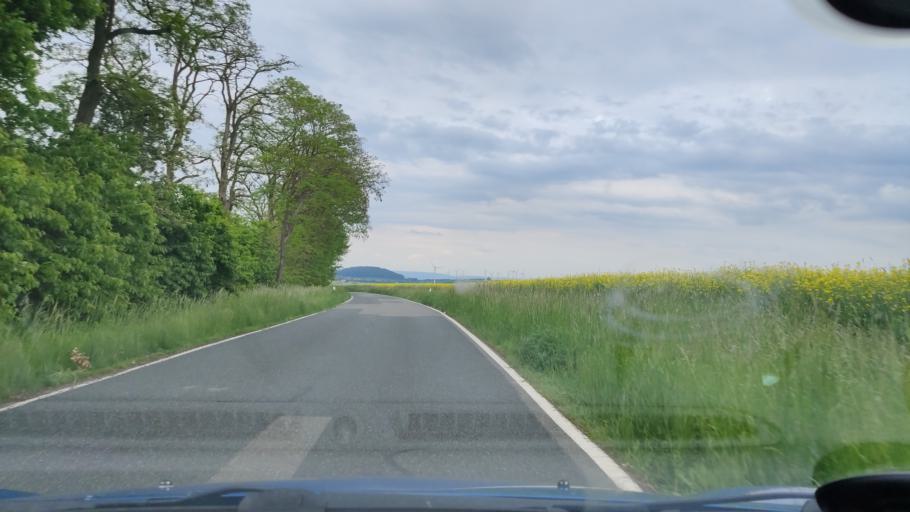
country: DE
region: Lower Saxony
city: Eimen
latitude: 51.8774
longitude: 9.8249
